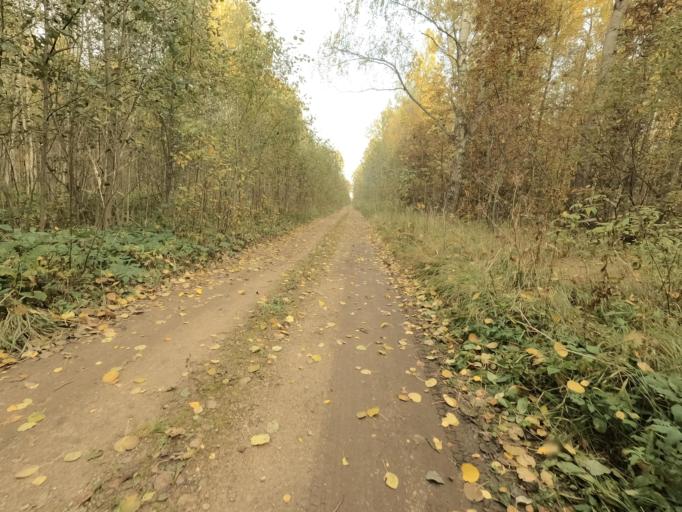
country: RU
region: Novgorod
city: Pankovka
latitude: 58.8800
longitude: 30.8280
